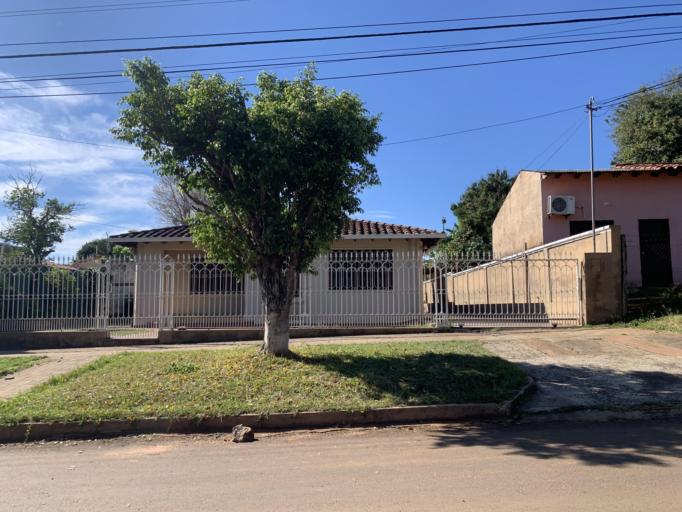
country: PY
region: Misiones
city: San Juan Bautista
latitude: -26.6661
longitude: -57.1404
